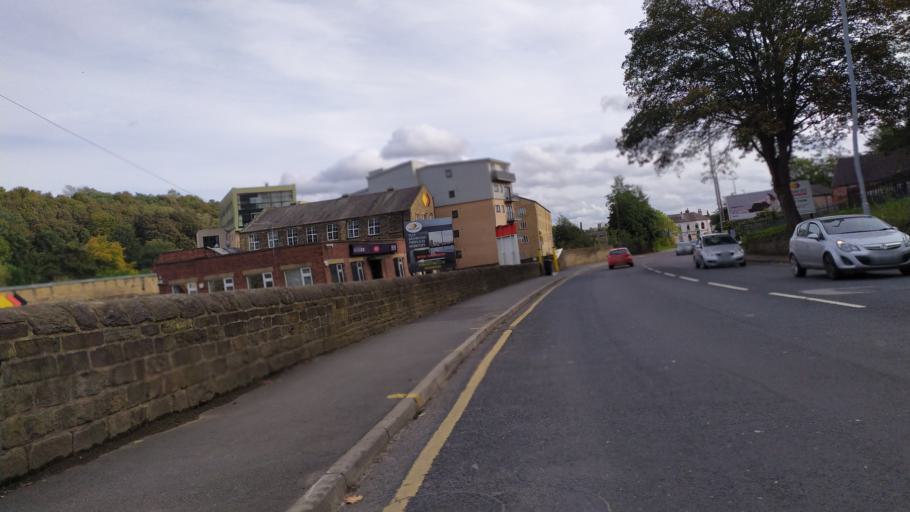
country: GB
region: England
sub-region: City and Borough of Leeds
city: Chapel Allerton
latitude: 53.8168
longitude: -1.5477
